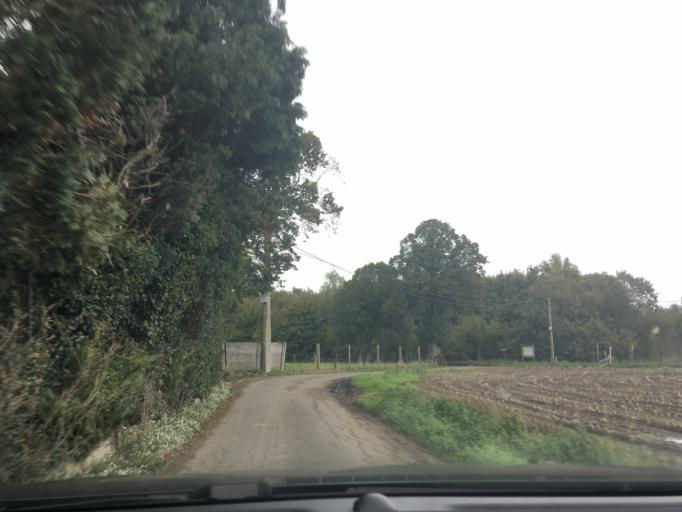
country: BE
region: Flanders
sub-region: Provincie West-Vlaanderen
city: Moorslede
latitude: 50.9109
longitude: 3.0646
